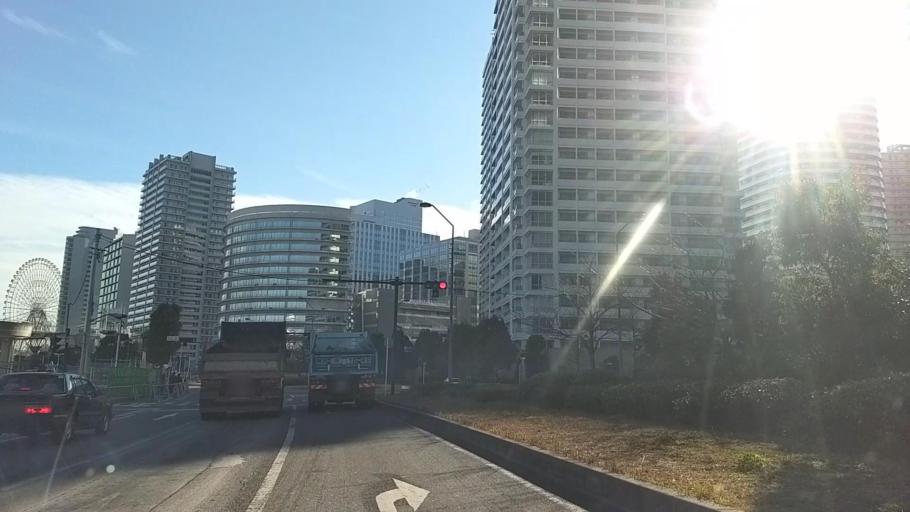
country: JP
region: Kanagawa
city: Yokohama
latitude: 35.4618
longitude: 139.6331
